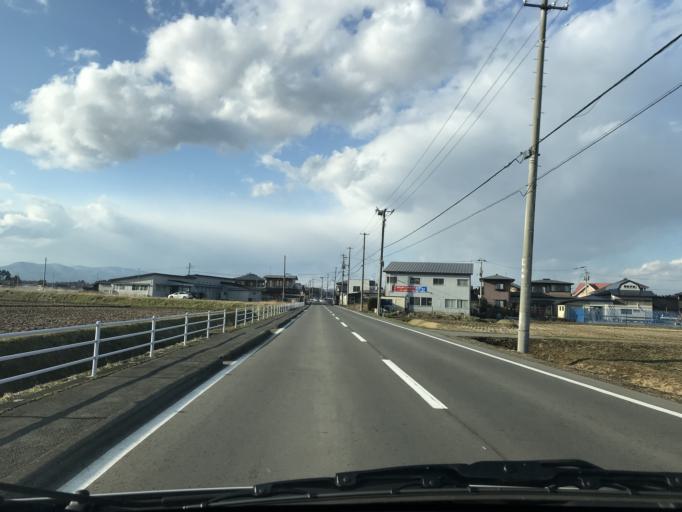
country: JP
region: Iwate
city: Kitakami
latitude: 39.3085
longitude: 141.0709
